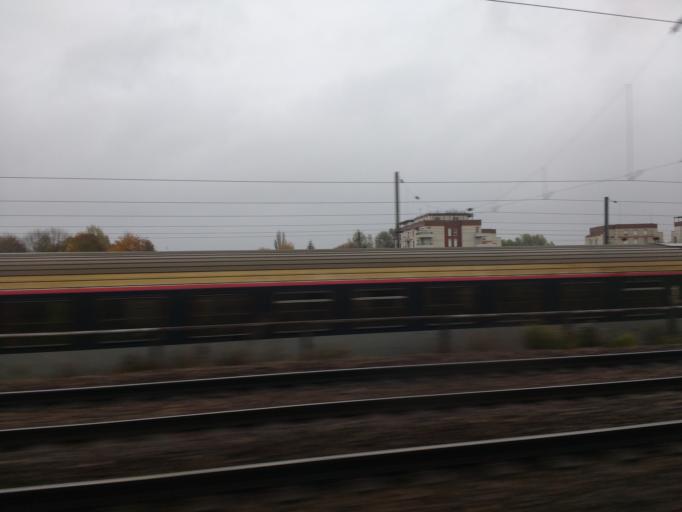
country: FR
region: Picardie
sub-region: Departement de la Somme
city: Rivery
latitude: 49.8885
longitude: 2.3248
